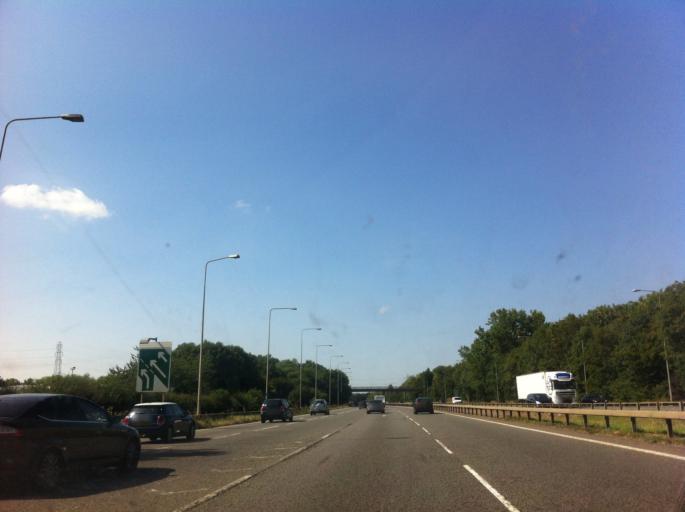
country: GB
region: England
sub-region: Northamptonshire
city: Northampton
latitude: 52.2430
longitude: -0.8404
